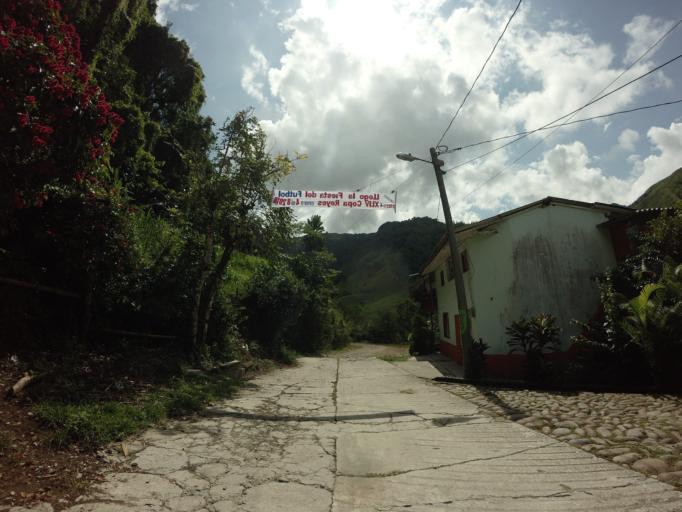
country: CO
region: Antioquia
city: Narino
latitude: 5.5196
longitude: -75.1921
